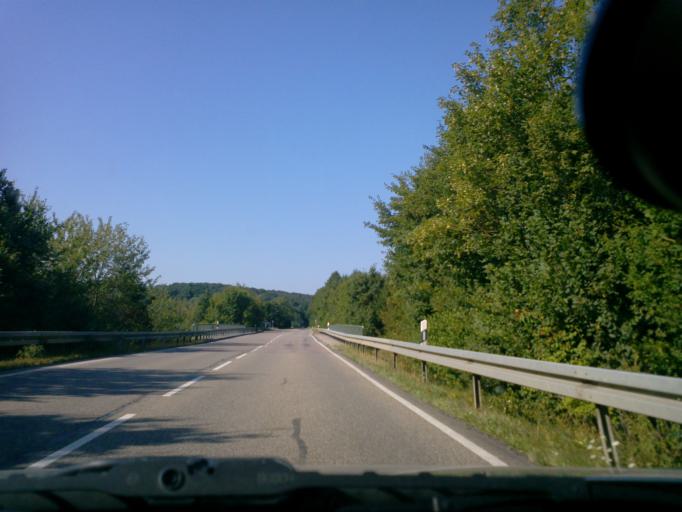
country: DE
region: Baden-Wuerttemberg
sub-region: Karlsruhe Region
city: Zaisenhausen
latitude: 49.0974
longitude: 8.8088
